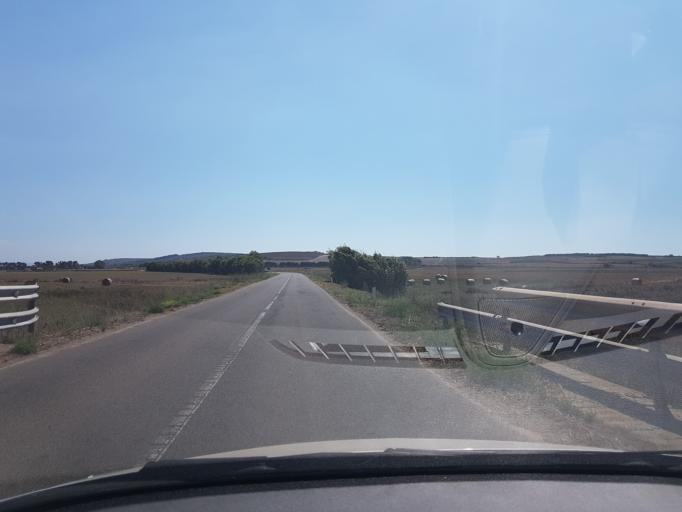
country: IT
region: Sardinia
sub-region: Provincia di Oristano
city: Nurachi
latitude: 39.9756
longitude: 8.4532
